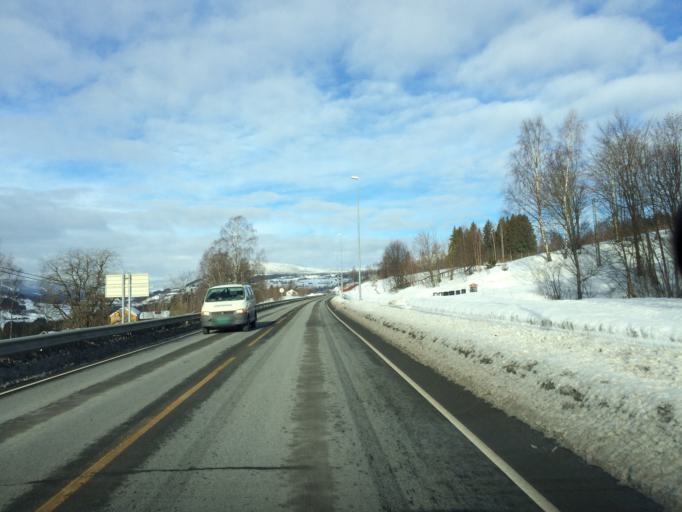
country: NO
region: Oppland
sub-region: Gausdal
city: Segalstad bru
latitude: 61.1923
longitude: 10.3152
